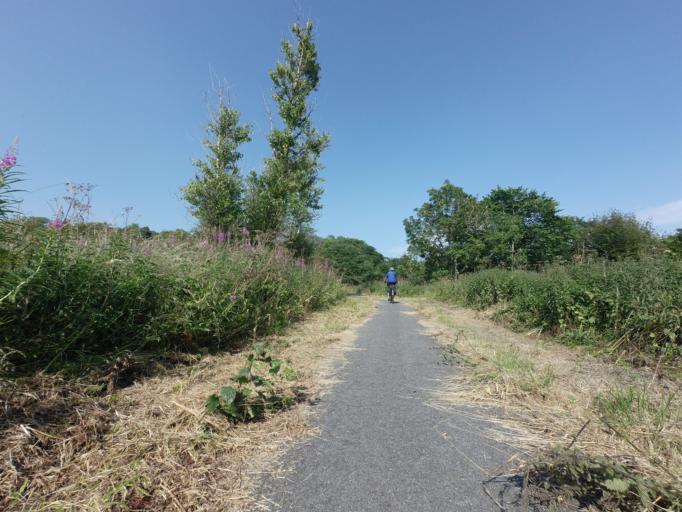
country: GB
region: Scotland
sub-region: Highland
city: Evanton
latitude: 57.6720
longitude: -4.3210
